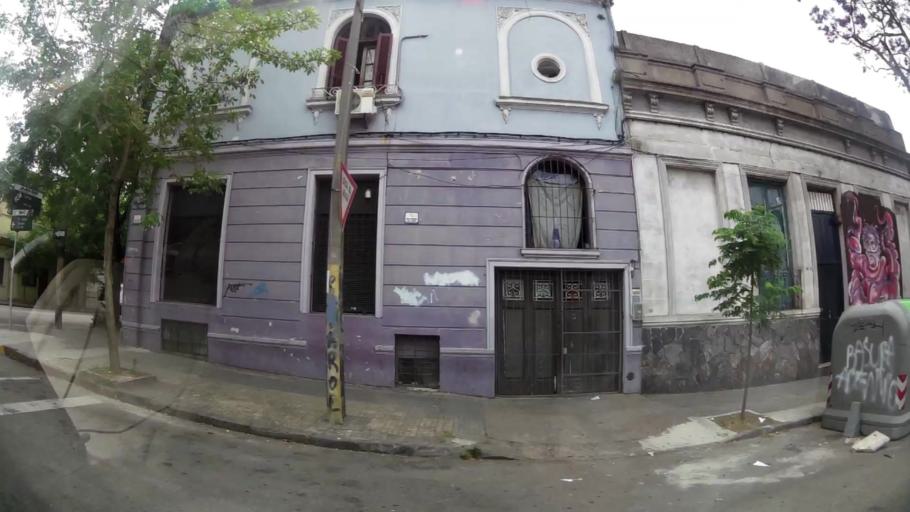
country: UY
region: Montevideo
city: Montevideo
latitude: -34.8943
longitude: -56.1714
